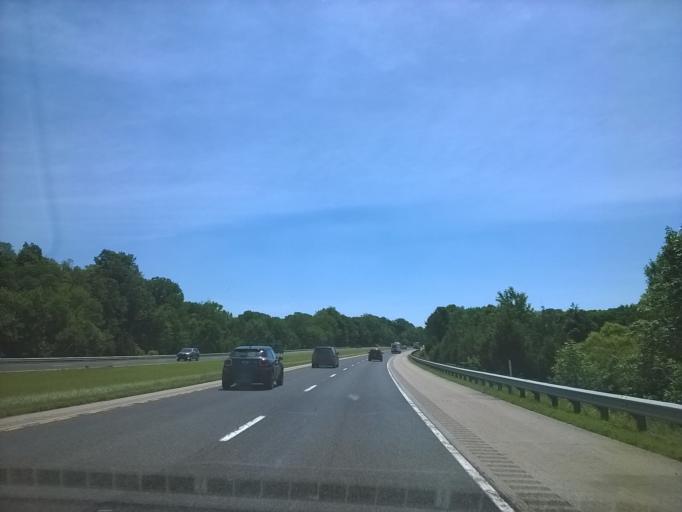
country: US
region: Indiana
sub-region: Ripley County
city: Batesville
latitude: 39.3141
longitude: -85.2285
